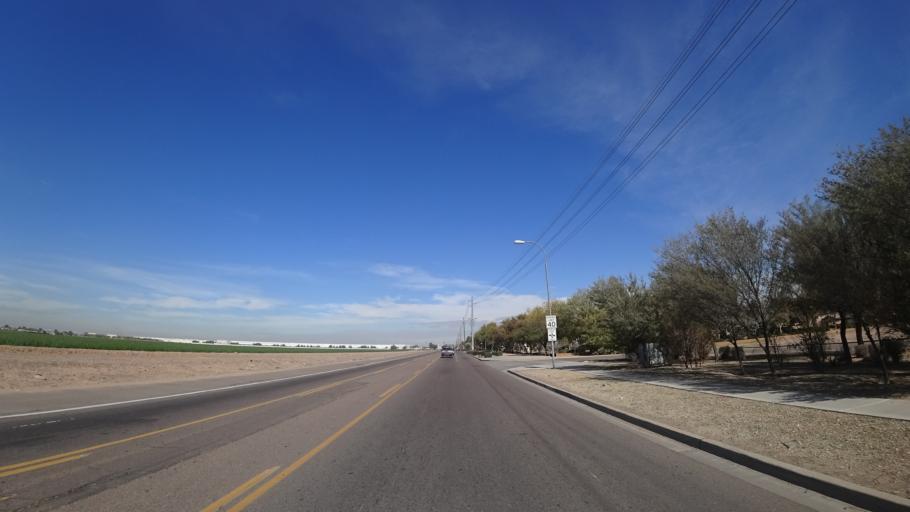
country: US
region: Arizona
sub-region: Maricopa County
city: Tolleson
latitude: 33.4241
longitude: -112.2040
